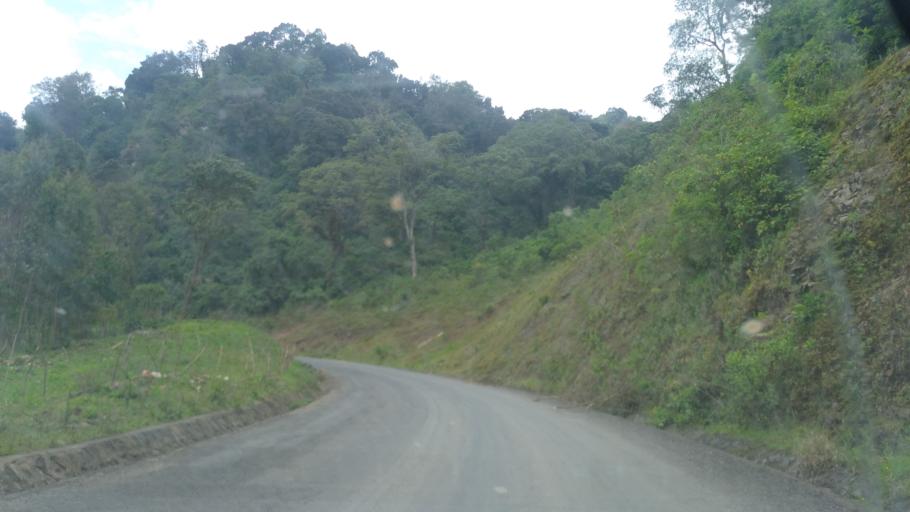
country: ET
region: Southern Nations, Nationalities, and People's Region
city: Bonga
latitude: 7.1144
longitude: 36.7249
